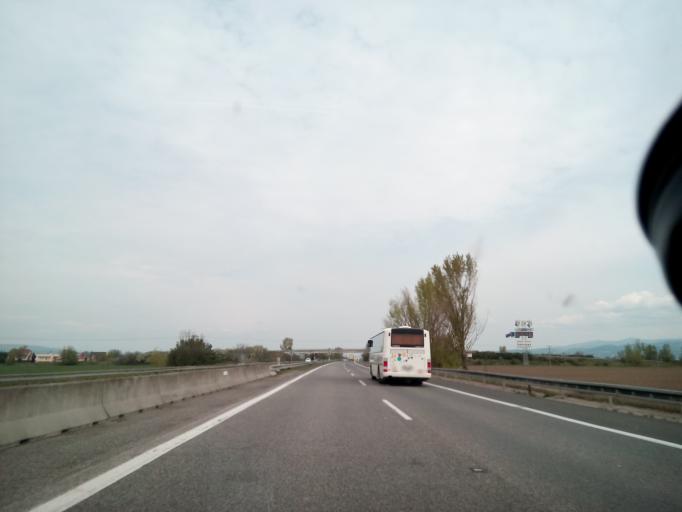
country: SK
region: Trnavsky
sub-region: Okres Trnava
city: Piestany
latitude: 48.6100
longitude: 17.7970
